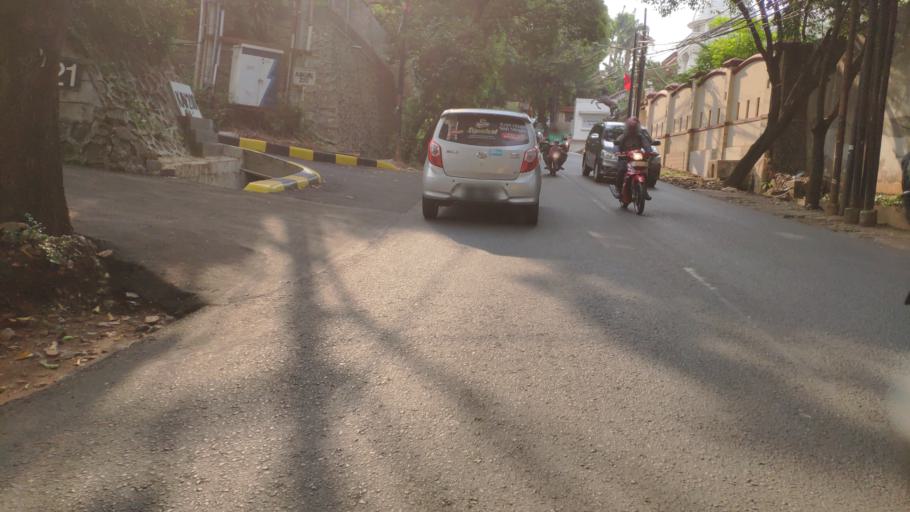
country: ID
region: West Java
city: Pamulang
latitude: -6.3108
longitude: 106.8067
